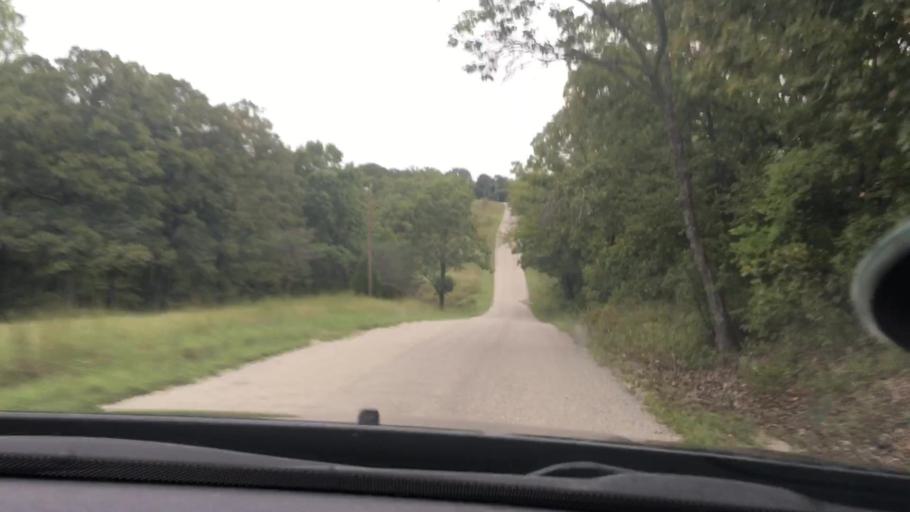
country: US
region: Oklahoma
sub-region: Pontotoc County
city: Byng
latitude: 34.8142
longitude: -96.5474
